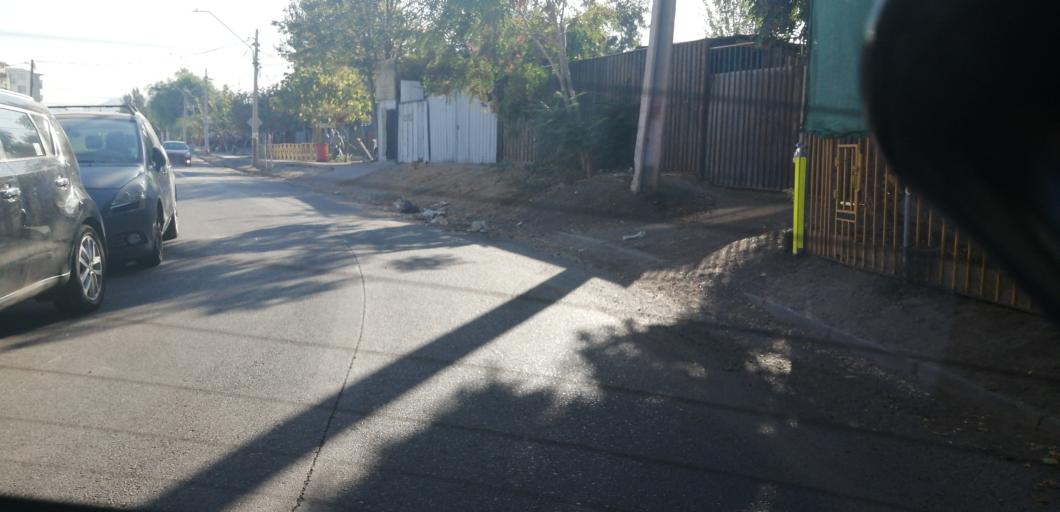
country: CL
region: Santiago Metropolitan
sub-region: Provincia de Santiago
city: Lo Prado
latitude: -33.4278
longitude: -70.7678
